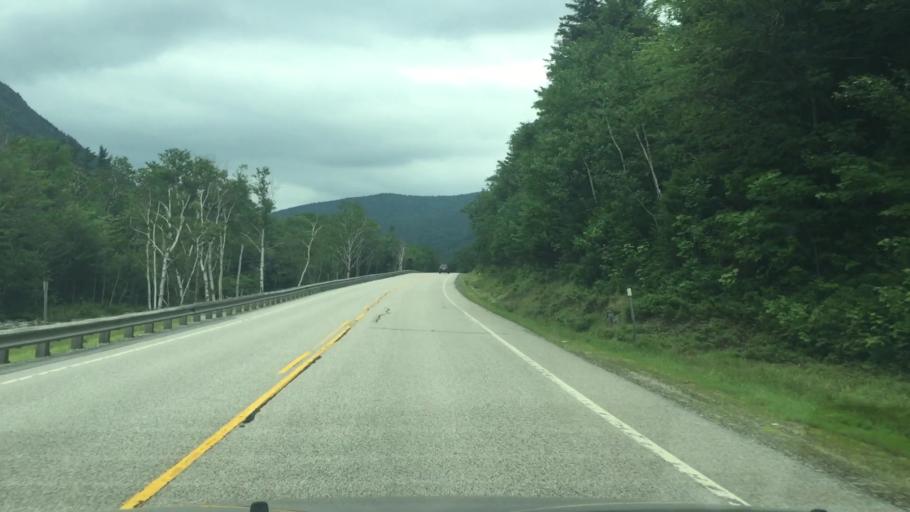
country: US
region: New Hampshire
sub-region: Grafton County
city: Deerfield
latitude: 44.1897
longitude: -71.4035
